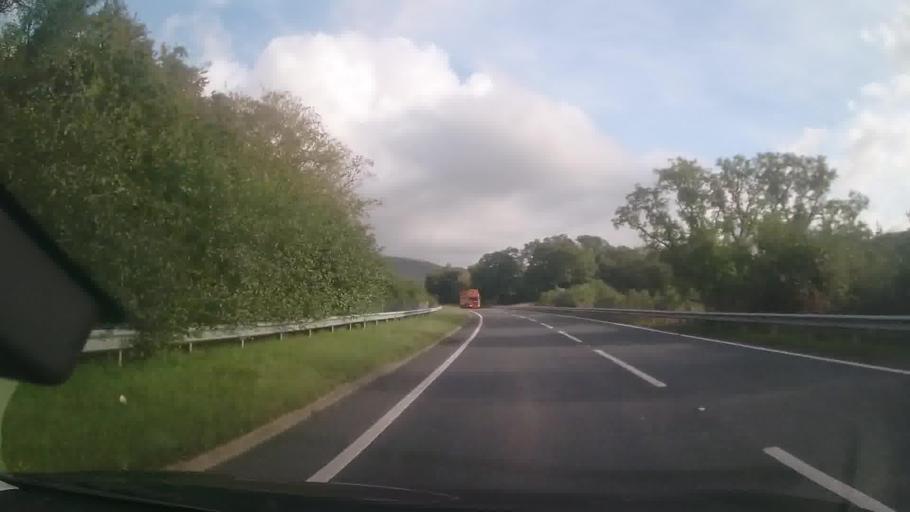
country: GB
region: Wales
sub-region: Gwynedd
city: Dolgellau
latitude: 52.7430
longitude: -3.8379
